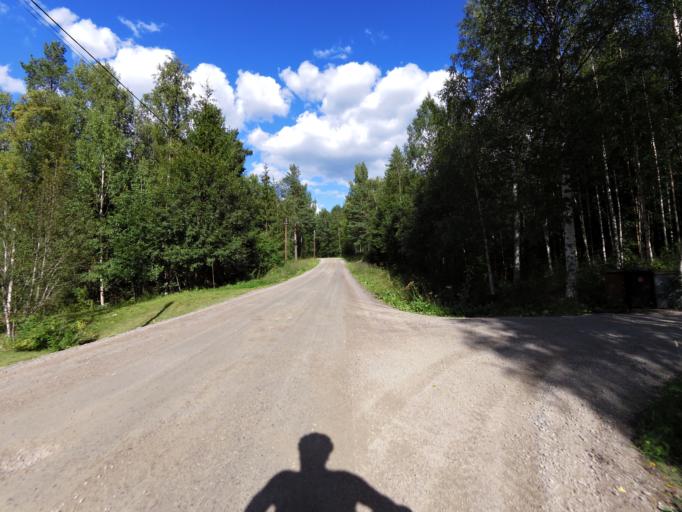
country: SE
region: Dalarna
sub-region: Faluns Kommun
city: Svardsjo
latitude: 60.6973
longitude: 15.8946
